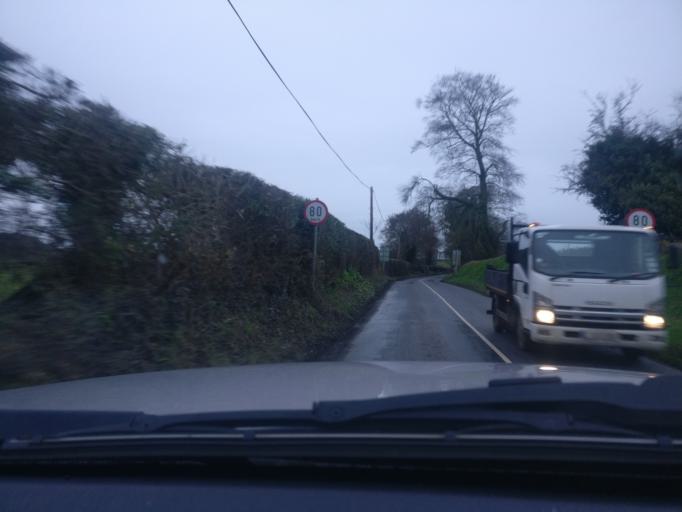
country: IE
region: Leinster
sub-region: An Mhi
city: Dunshaughlin
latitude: 53.4888
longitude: -6.6077
